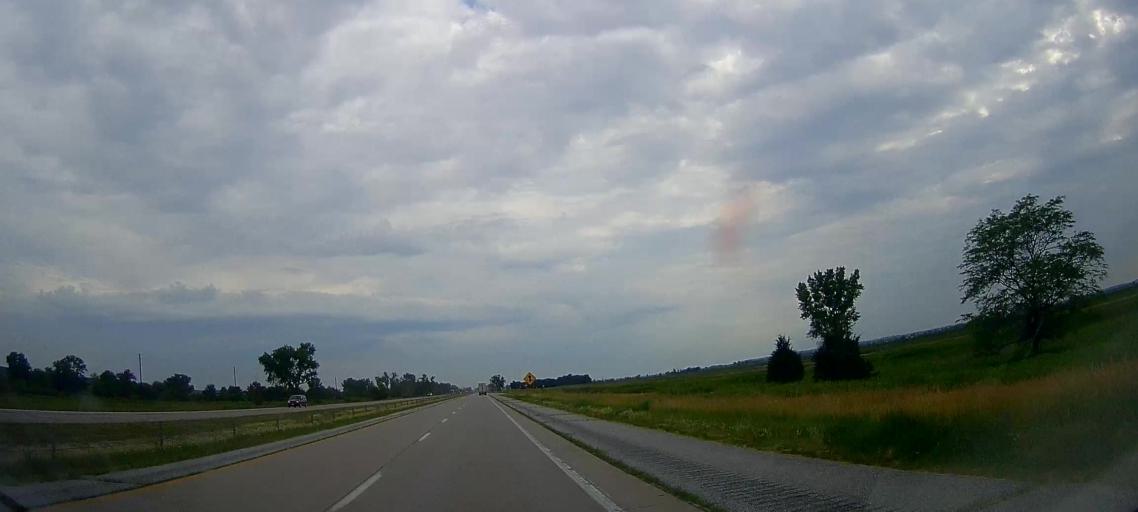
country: US
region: Iowa
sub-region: Harrison County
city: Missouri Valley
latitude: 41.4891
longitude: -95.9009
